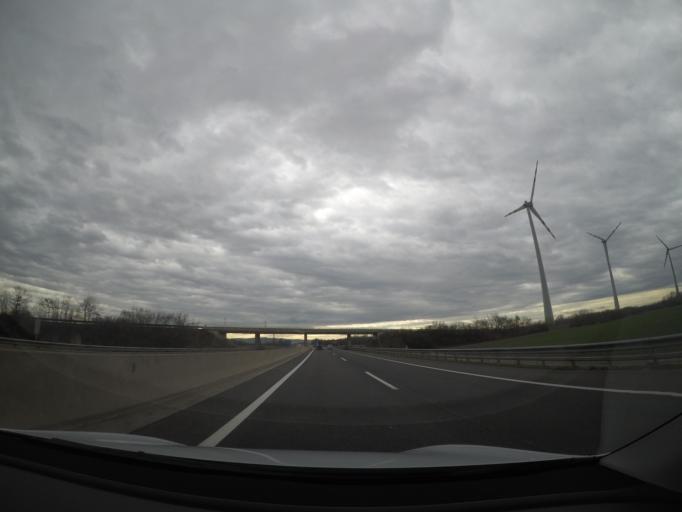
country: AT
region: Lower Austria
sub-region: Politischer Bezirk Baden
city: Ebreichsdorf
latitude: 47.9397
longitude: 16.3762
